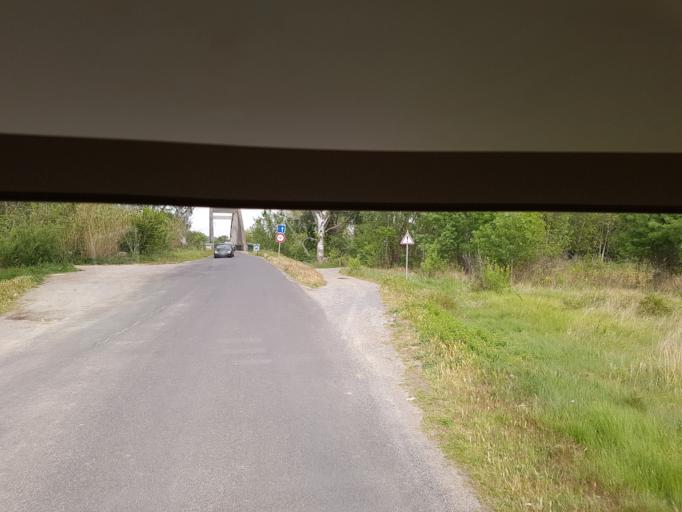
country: FR
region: Languedoc-Roussillon
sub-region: Departement de l'Aude
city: Fleury
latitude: 43.2437
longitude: 3.1517
